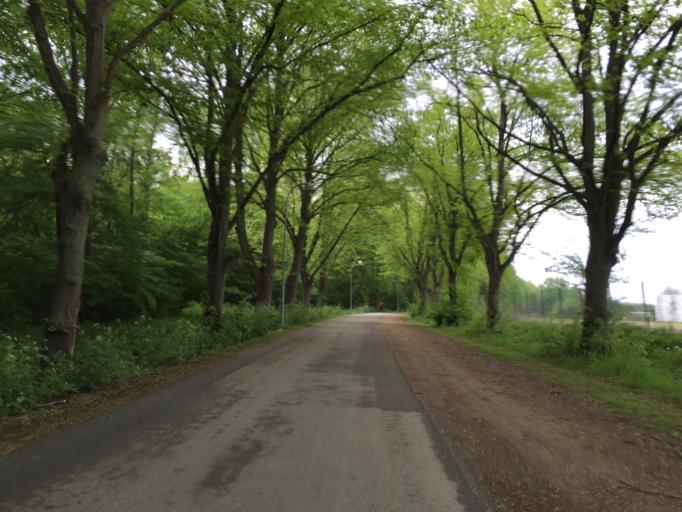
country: DK
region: Capital Region
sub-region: Brondby Kommune
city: Brondbyvester
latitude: 55.6276
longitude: 12.4403
